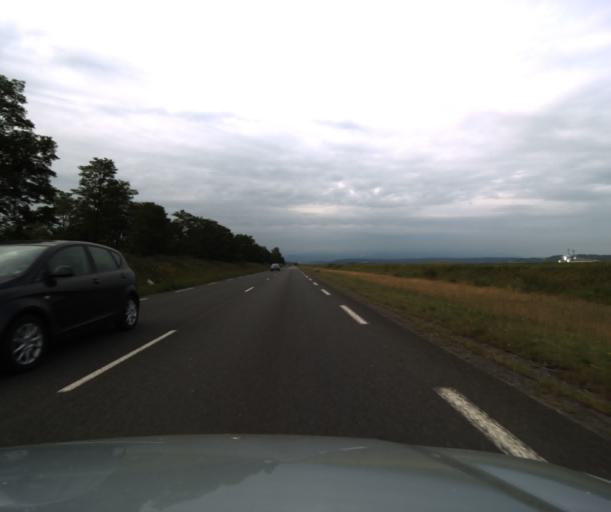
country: FR
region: Midi-Pyrenees
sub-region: Departement des Hautes-Pyrenees
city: Juillan
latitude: 43.2130
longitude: 0.0136
